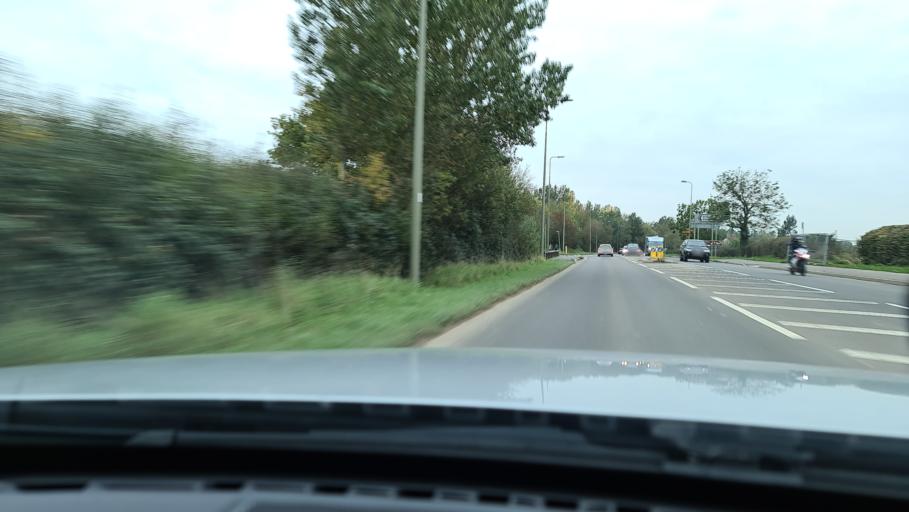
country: GB
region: England
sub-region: Oxfordshire
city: Bicester
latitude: 51.8801
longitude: -1.1278
